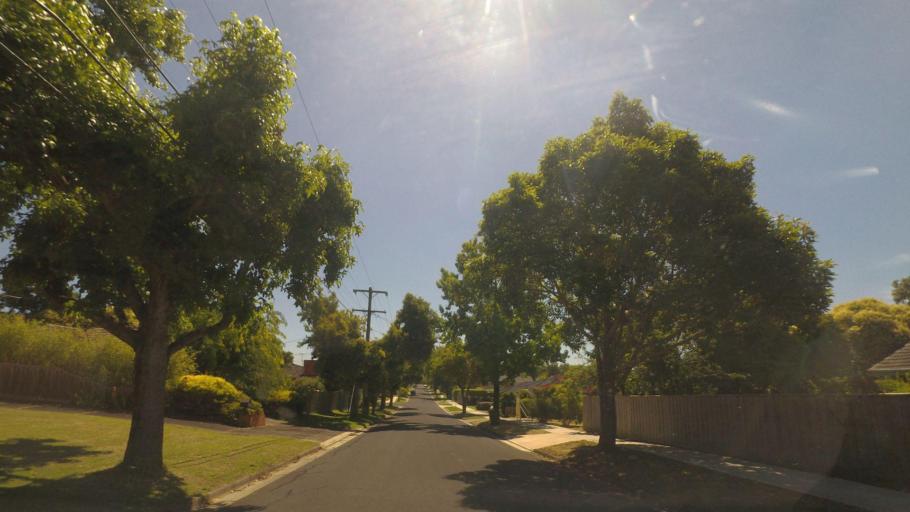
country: AU
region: Victoria
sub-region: Maroondah
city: Ringwood East
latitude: -37.7973
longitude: 145.2327
